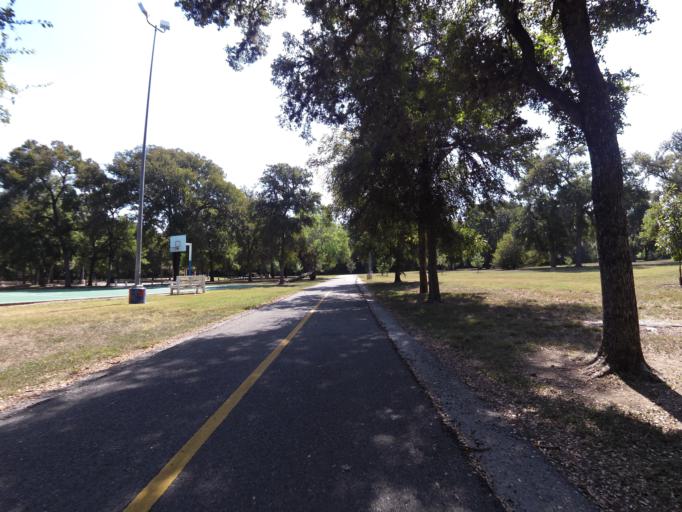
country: US
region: Texas
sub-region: Bexar County
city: Kirby
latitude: 29.4150
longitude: -98.4174
